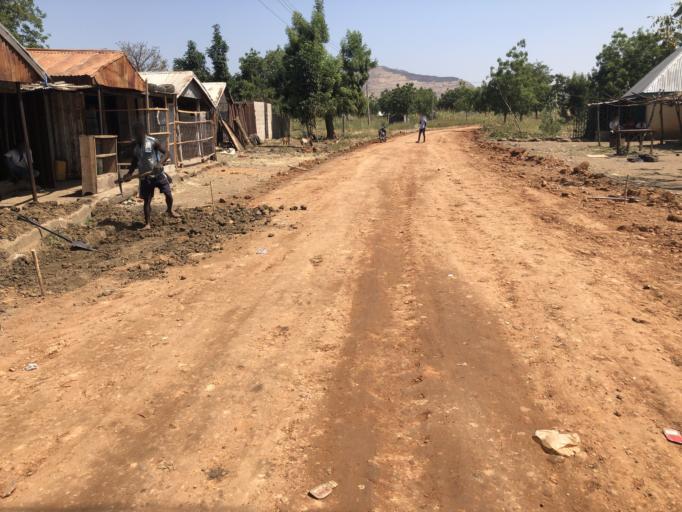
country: NG
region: Adamawa
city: Numan
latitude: 9.6837
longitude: 11.8682
